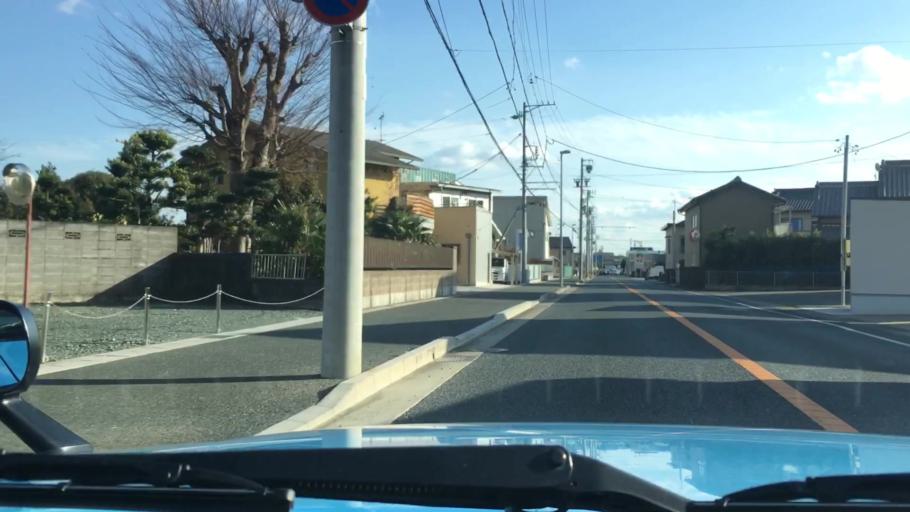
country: JP
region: Shizuoka
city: Hamamatsu
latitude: 34.7549
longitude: 137.6704
